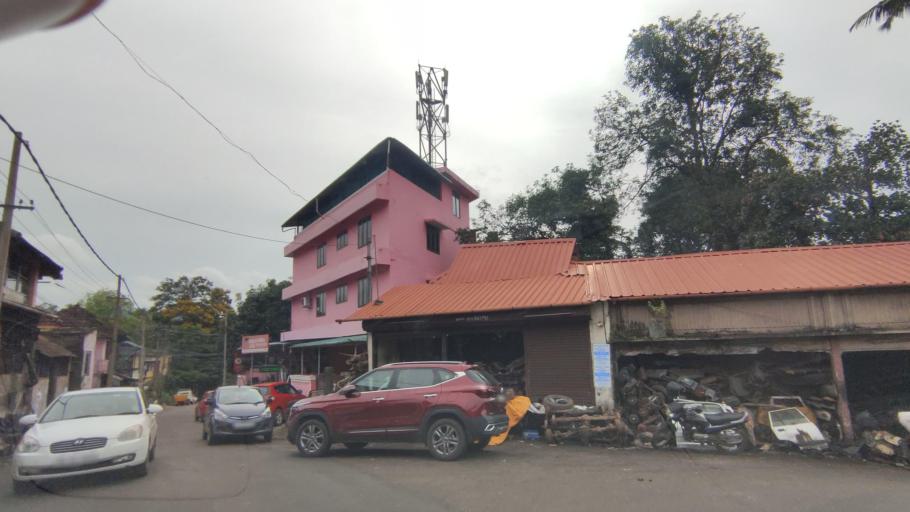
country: IN
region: Kerala
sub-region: Kottayam
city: Kottayam
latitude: 9.5873
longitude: 76.5200
